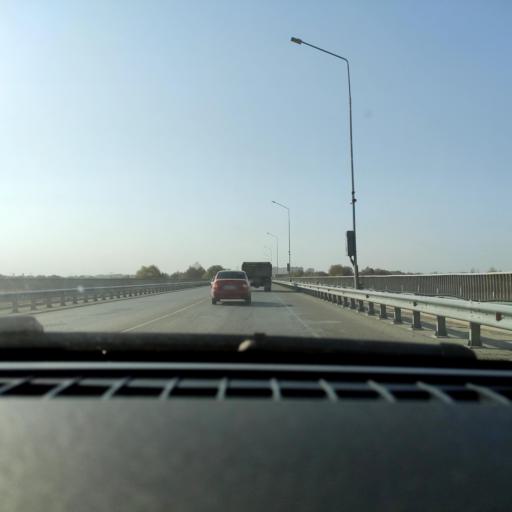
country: RU
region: Voronezj
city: Somovo
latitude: 51.6852
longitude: 39.3506
